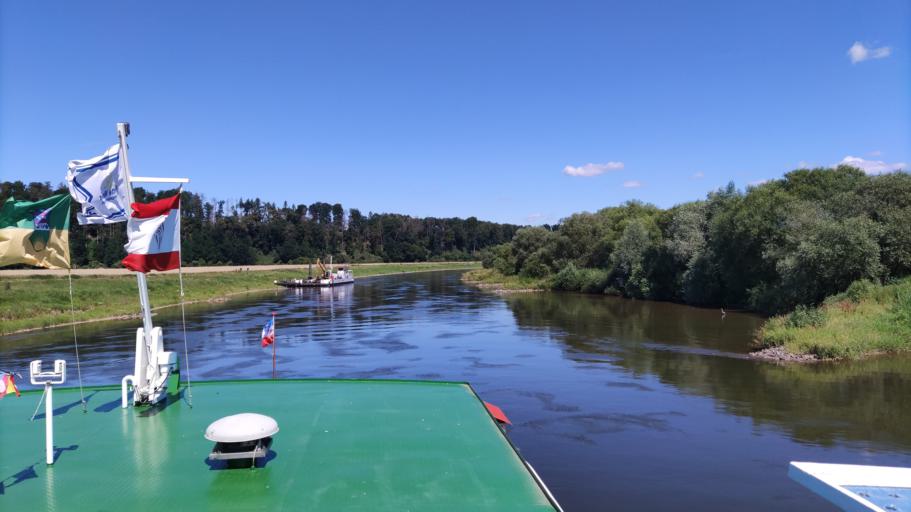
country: DE
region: Lower Saxony
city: Furstenberg
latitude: 51.7166
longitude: 9.3885
